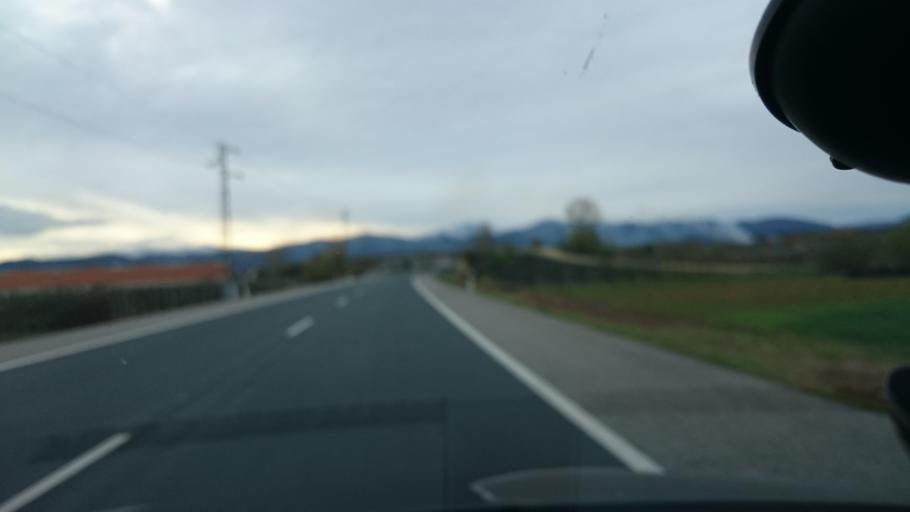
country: ES
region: Castille and Leon
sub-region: Provincia de Leon
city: Carracedelo
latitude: 42.5632
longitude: -6.7195
